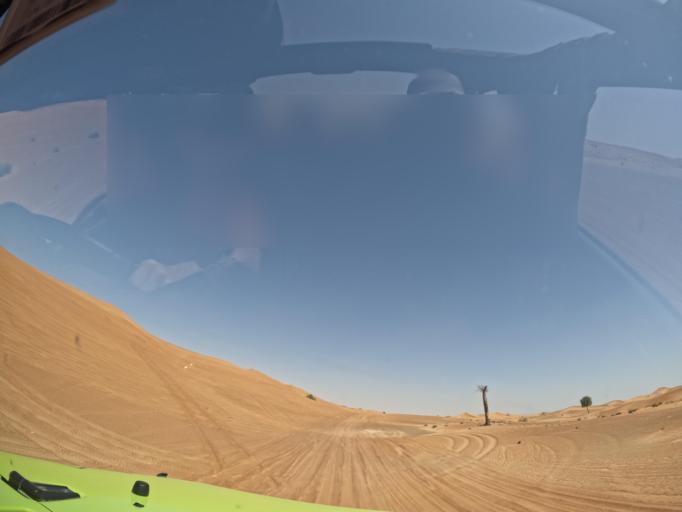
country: AE
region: Ash Shariqah
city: Adh Dhayd
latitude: 24.9939
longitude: 55.7246
